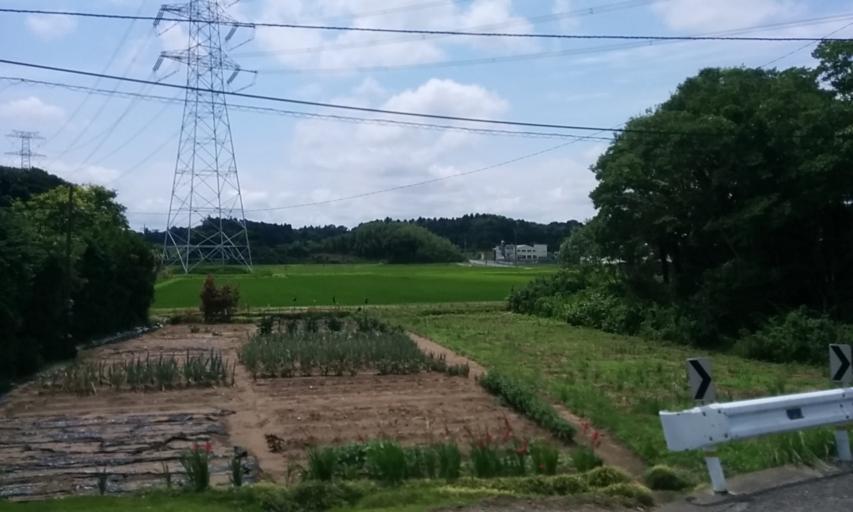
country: JP
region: Ibaraki
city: Inashiki
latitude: 35.8865
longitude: 140.3876
